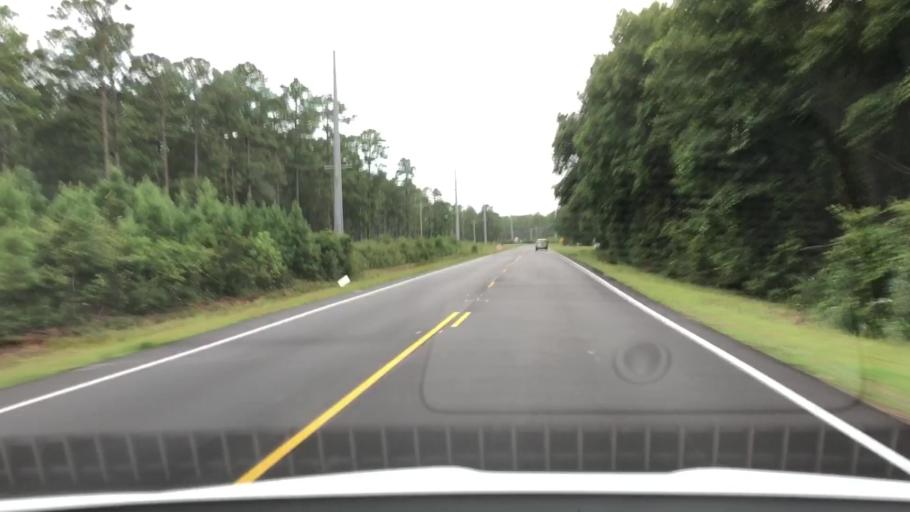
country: US
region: North Carolina
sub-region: Onslow County
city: Swansboro
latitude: 34.8041
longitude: -77.1327
